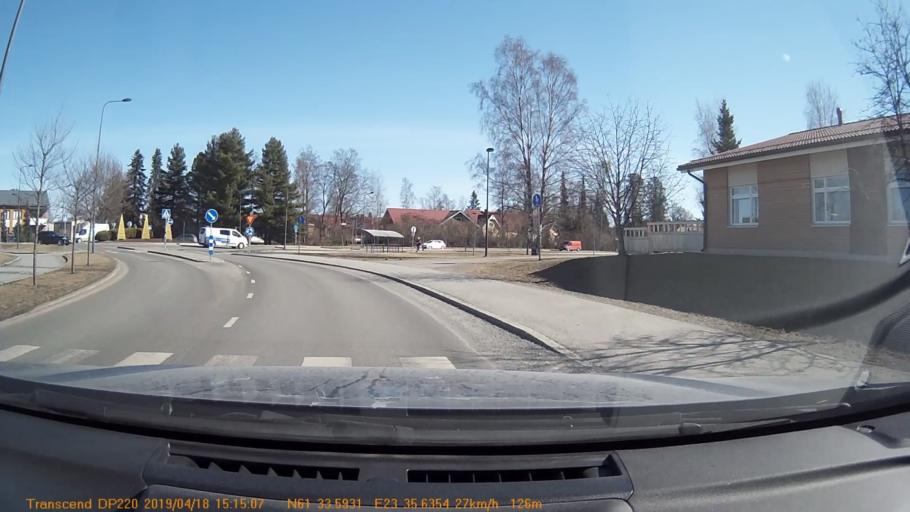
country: FI
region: Pirkanmaa
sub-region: Tampere
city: Yloejaervi
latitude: 61.5599
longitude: 23.5942
